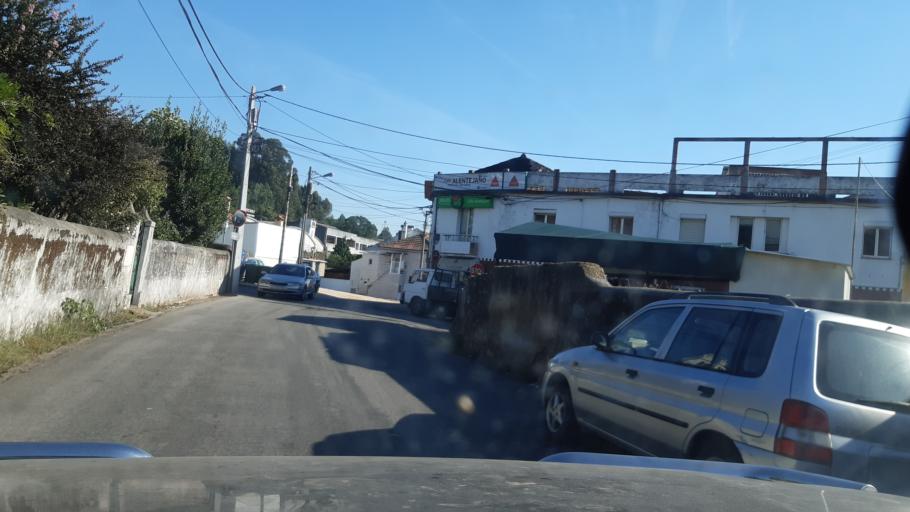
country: PT
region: Aveiro
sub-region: Agueda
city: Agueda
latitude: 40.5709
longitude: -8.4342
